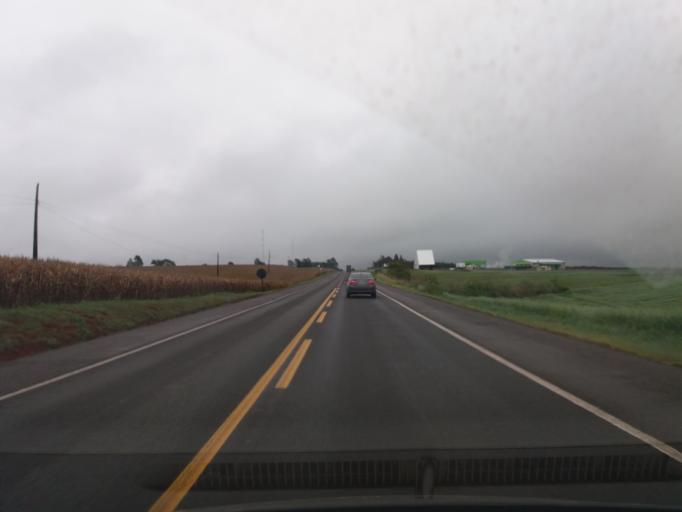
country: BR
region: Parana
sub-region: Ampere
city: Ampere
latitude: -25.9105
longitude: -53.4342
